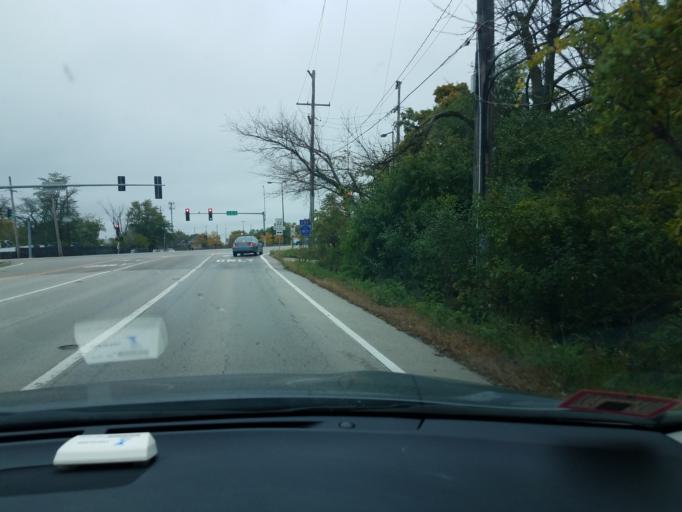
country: US
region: Illinois
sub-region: Lake County
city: Vernon Hills
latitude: 42.1951
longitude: -87.9553
